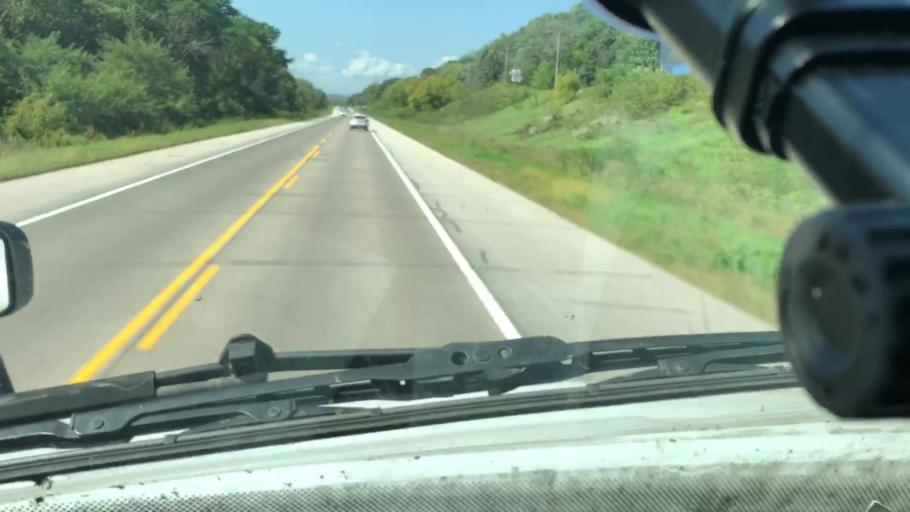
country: US
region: Minnesota
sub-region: Winona County
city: Winona
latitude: 44.0703
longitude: -91.6064
